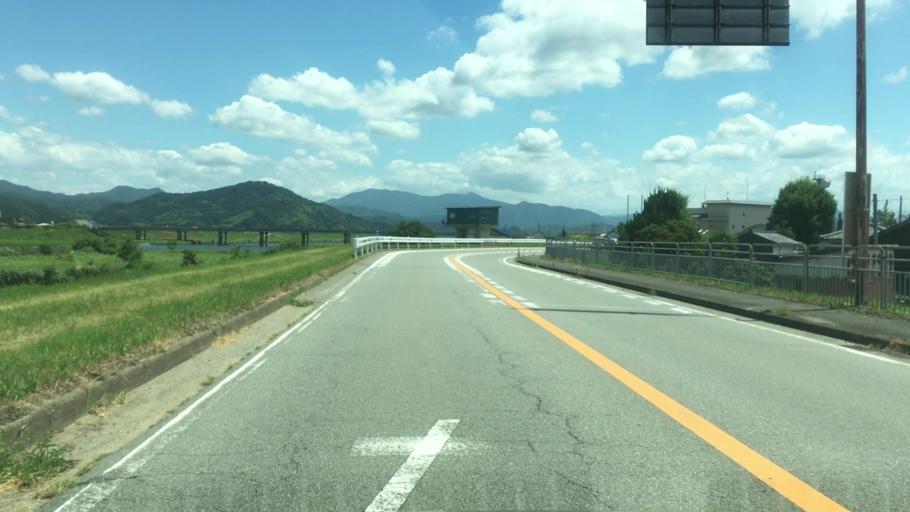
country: JP
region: Hyogo
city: Toyooka
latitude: 35.5484
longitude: 134.8259
